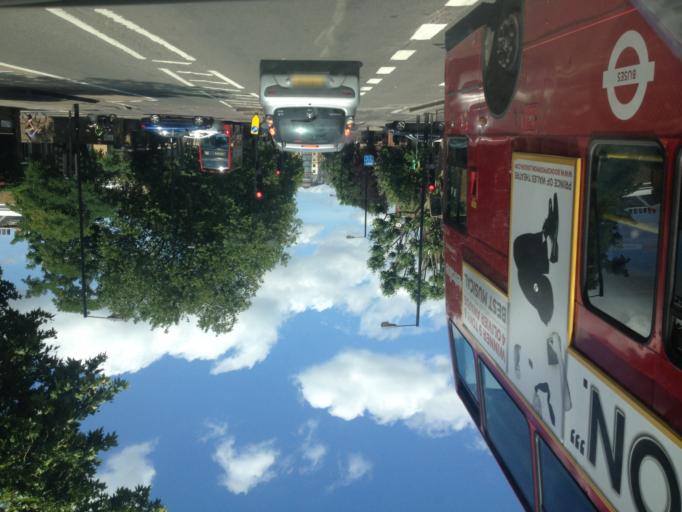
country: GB
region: England
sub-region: Greater London
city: Belsize Park
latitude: 51.5332
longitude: -0.1873
